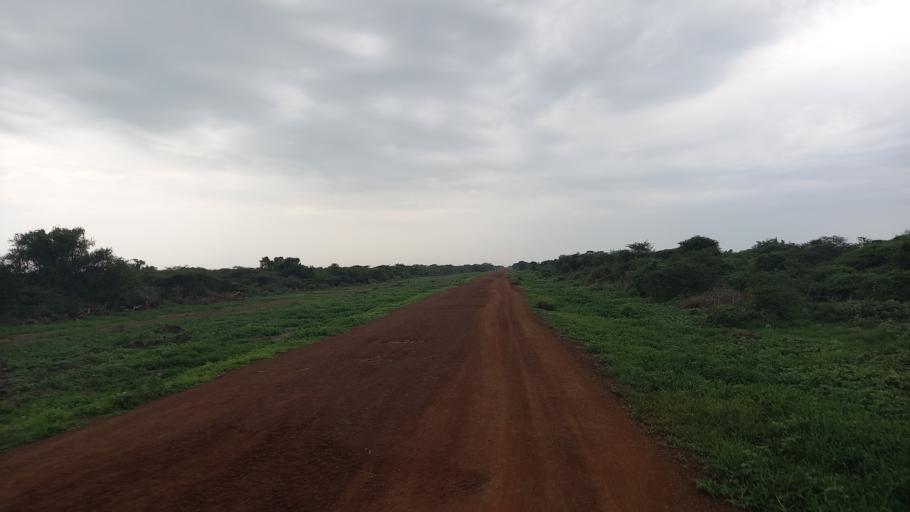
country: ET
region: Gambela
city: Gambela
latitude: 8.3384
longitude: 33.9298
